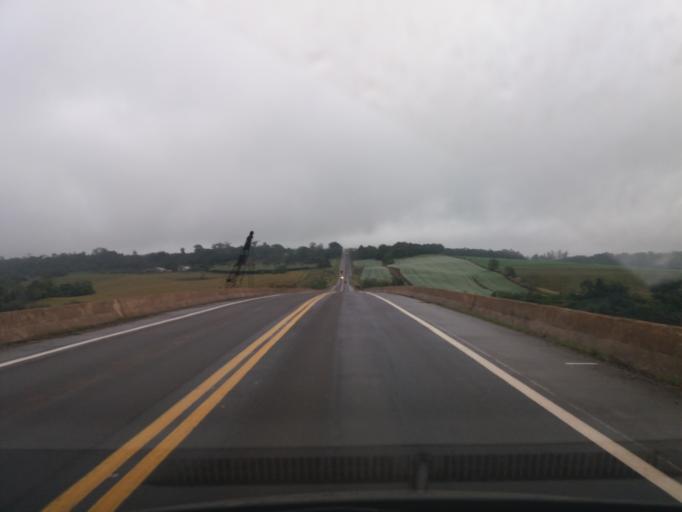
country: BR
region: Parana
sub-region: Realeza
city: Realeza
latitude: -25.5635
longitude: -53.5784
